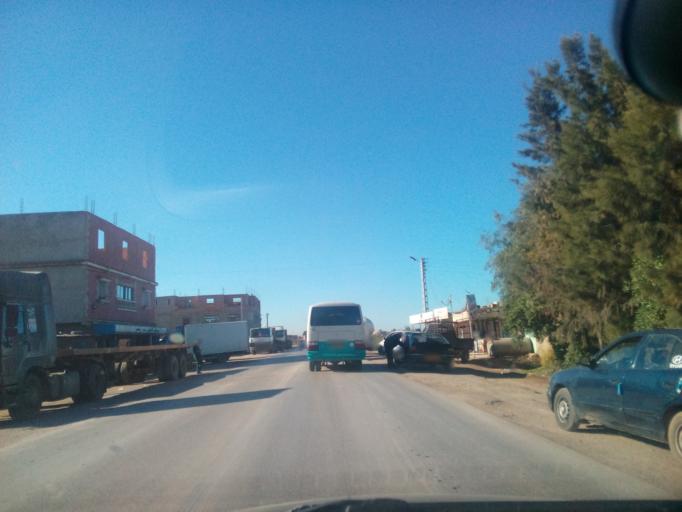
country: DZ
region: Relizane
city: Djidiouia
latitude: 35.8962
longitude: 0.6934
